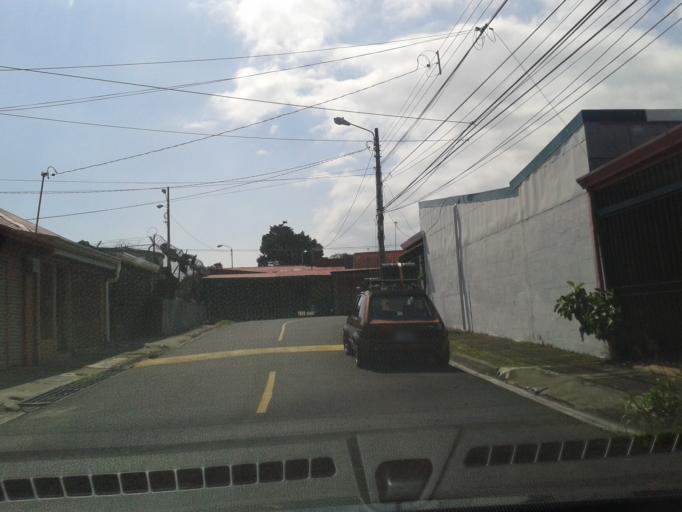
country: CR
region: Heredia
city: San Francisco
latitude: 9.9924
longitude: -84.1379
